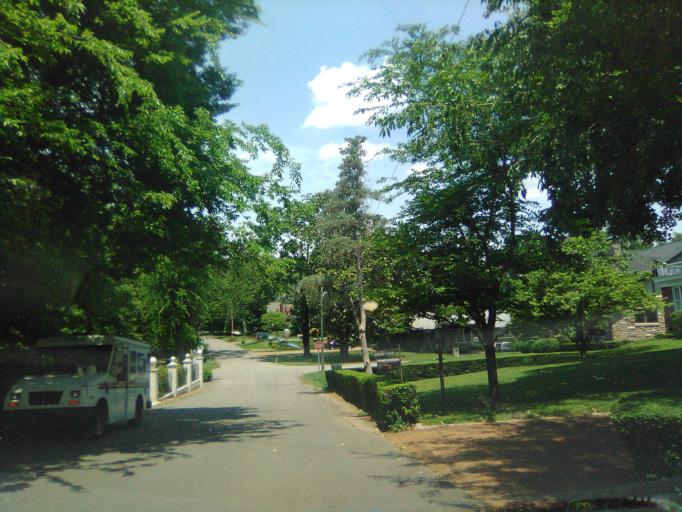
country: US
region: Tennessee
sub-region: Davidson County
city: Belle Meade
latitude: 36.1328
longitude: -86.8365
